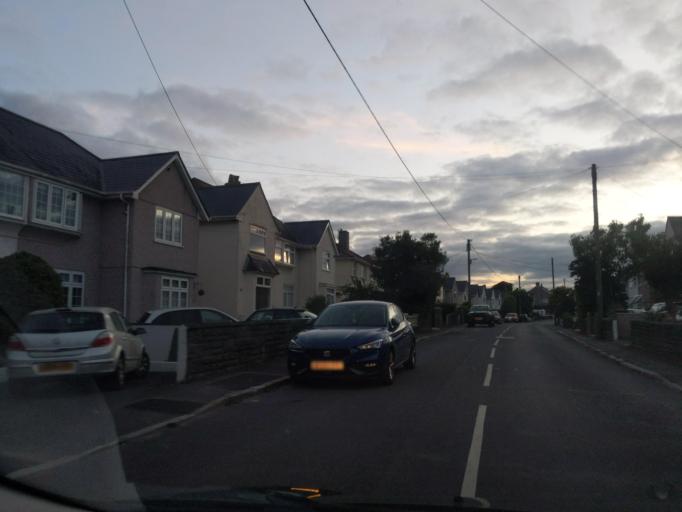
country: GB
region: England
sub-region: Plymouth
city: Plymstock
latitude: 50.3600
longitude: -4.0968
